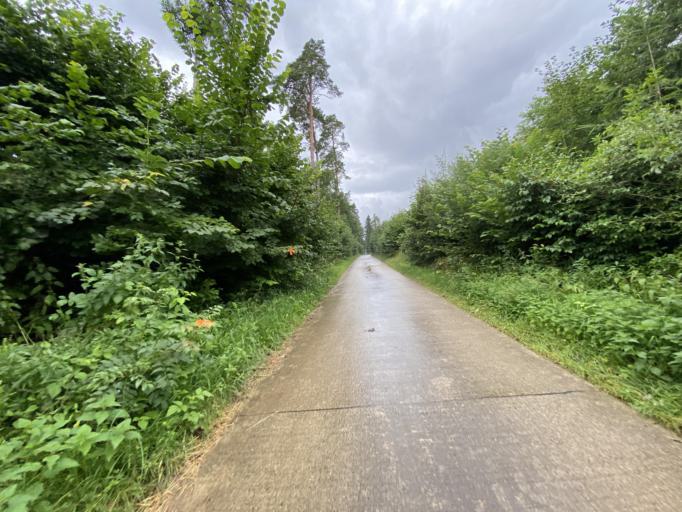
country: DE
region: Baden-Wuerttemberg
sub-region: Tuebingen Region
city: Bingen
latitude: 48.1185
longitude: 9.2526
